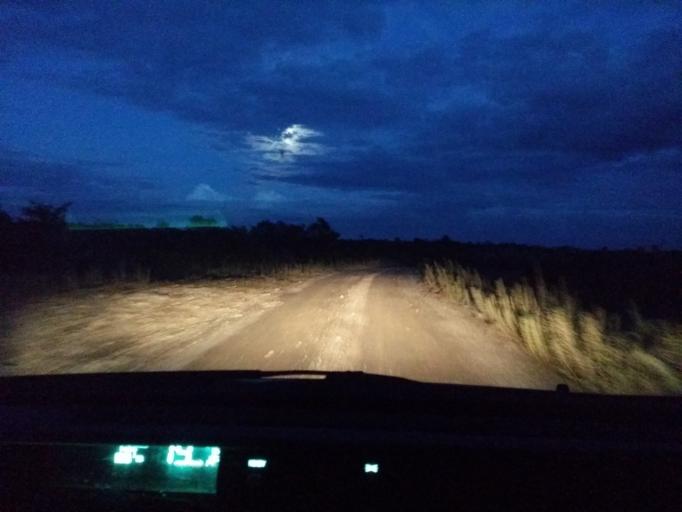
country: SE
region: Kalmar
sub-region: Borgholms Kommun
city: Borgholm
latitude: 57.1131
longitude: 16.8977
